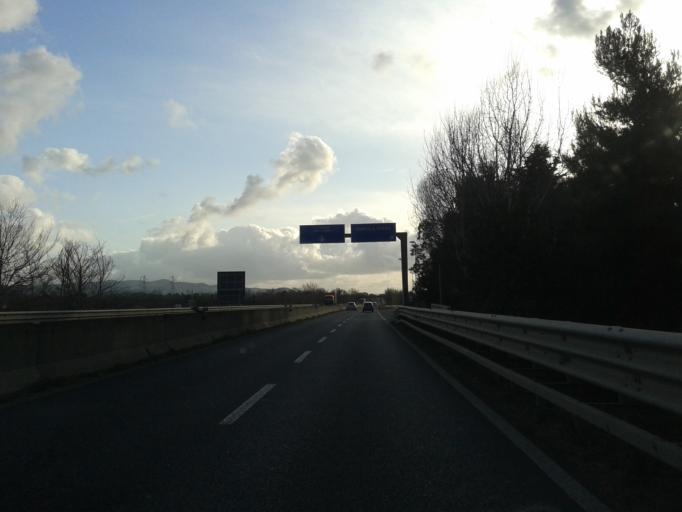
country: IT
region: Tuscany
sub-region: Provincia di Livorno
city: Livorno
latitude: 43.5588
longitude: 10.3453
